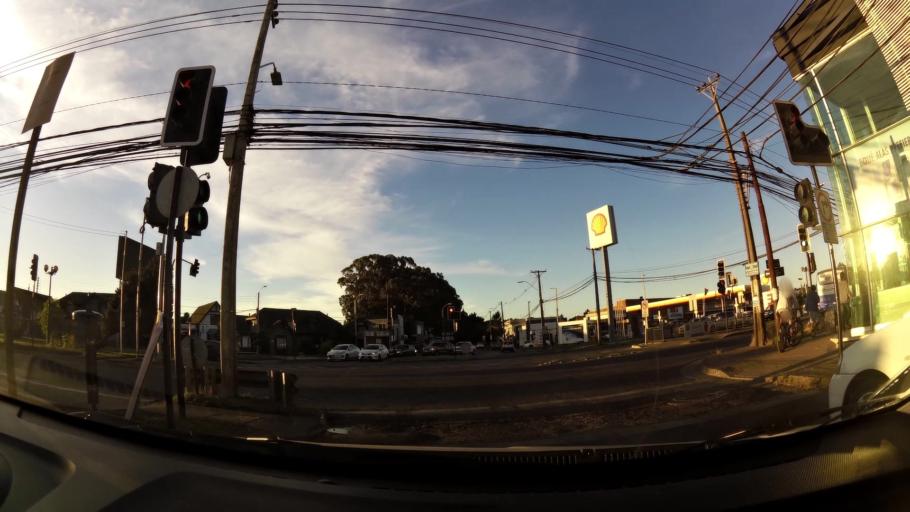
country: CL
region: Biobio
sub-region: Provincia de Concepcion
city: Concepcion
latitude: -36.8439
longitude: -73.0946
